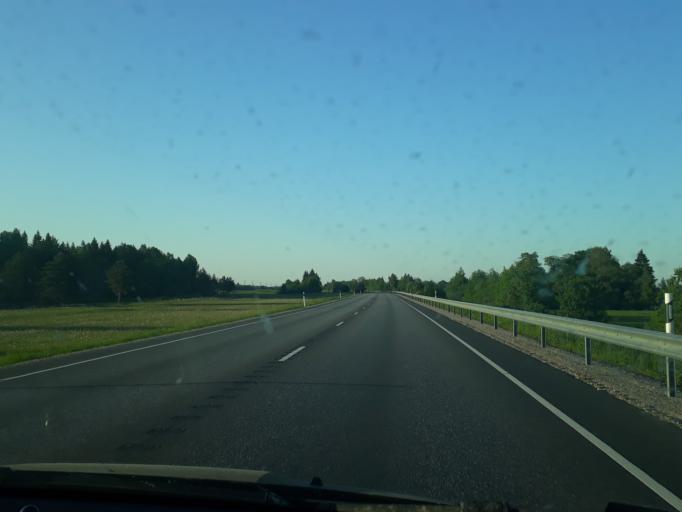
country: EE
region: Paernumaa
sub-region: Tootsi vald
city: Tootsi
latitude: 58.5802
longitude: 24.8905
